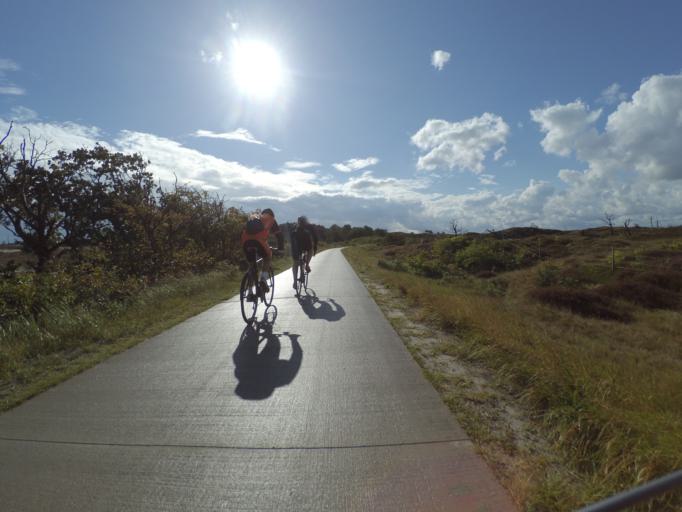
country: NL
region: North Holland
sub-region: Gemeente Bergen
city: Egmond aan Zee
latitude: 52.7093
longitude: 4.6655
